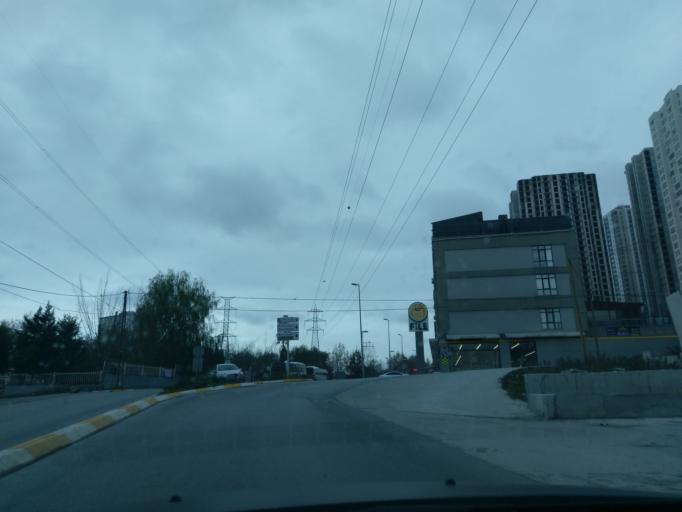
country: TR
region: Istanbul
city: Esenyurt
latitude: 41.0159
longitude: 28.6733
